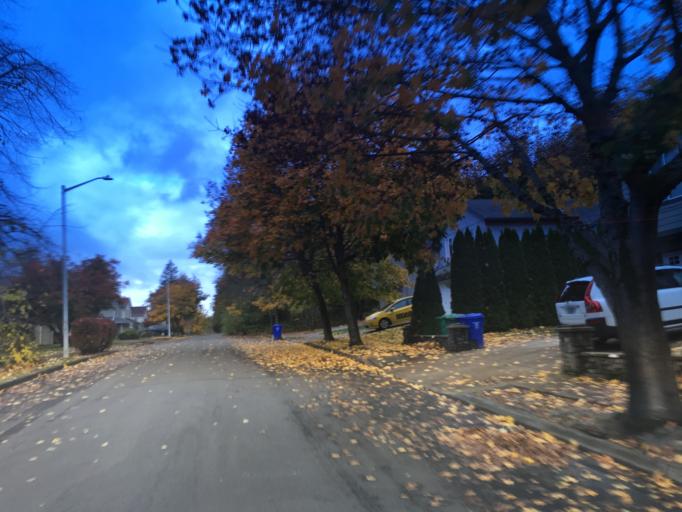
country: US
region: Oregon
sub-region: Multnomah County
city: Fairview
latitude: 45.5220
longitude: -122.4381
